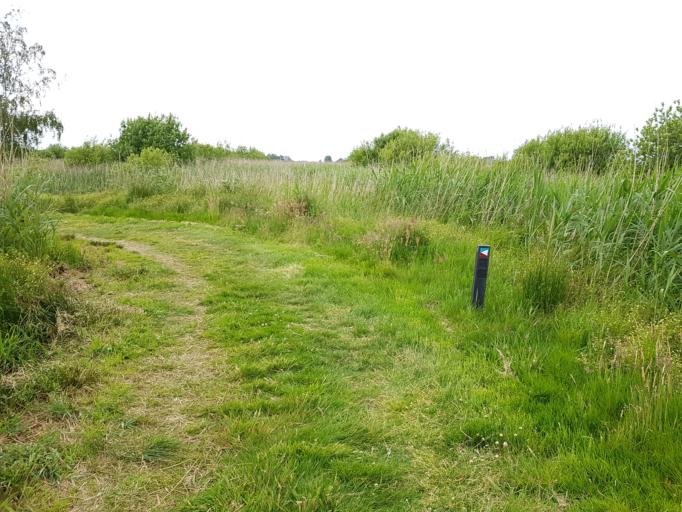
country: NL
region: Friesland
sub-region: Gemeente Tytsjerksteradiel
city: Garyp
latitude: 53.1437
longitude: 5.9442
